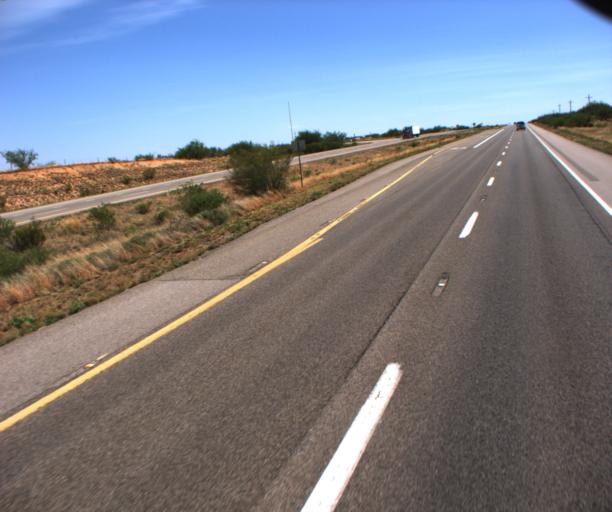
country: US
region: Arizona
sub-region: Cochise County
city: Whetstone
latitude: 31.9216
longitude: -110.3413
